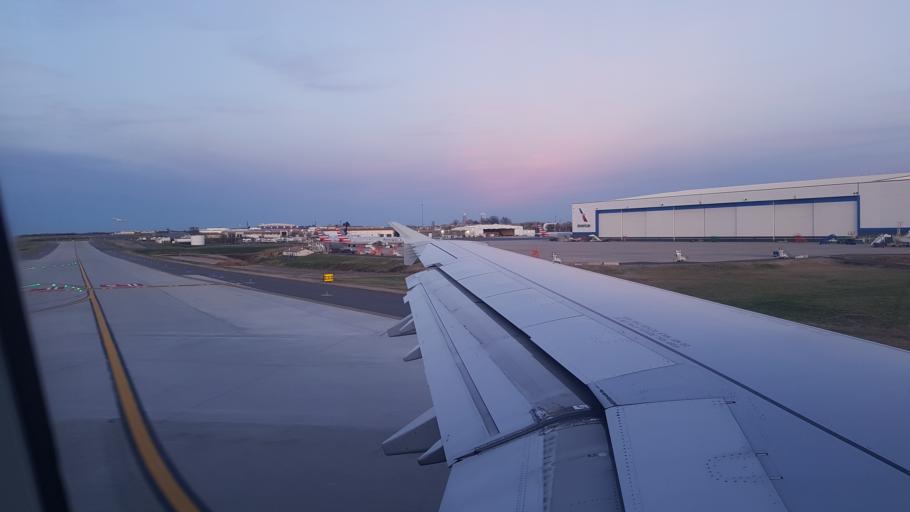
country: US
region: North Carolina
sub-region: Gaston County
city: Belmont
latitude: 35.2079
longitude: -80.9494
